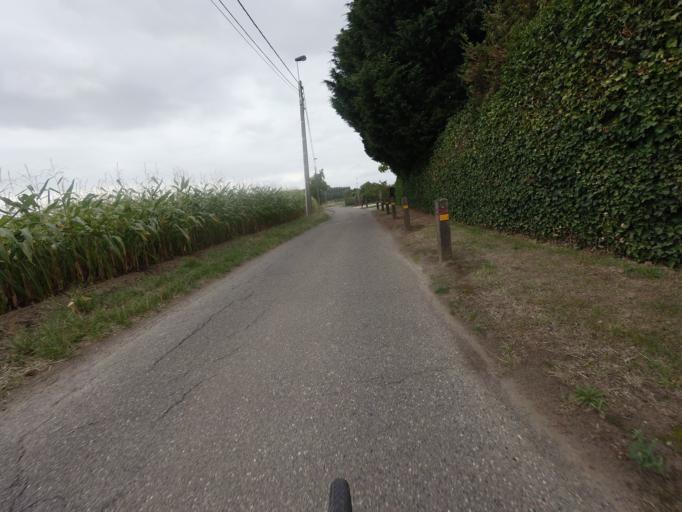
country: BE
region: Flanders
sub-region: Provincie Vlaams-Brabant
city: Bertem
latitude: 50.9004
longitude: 4.5949
